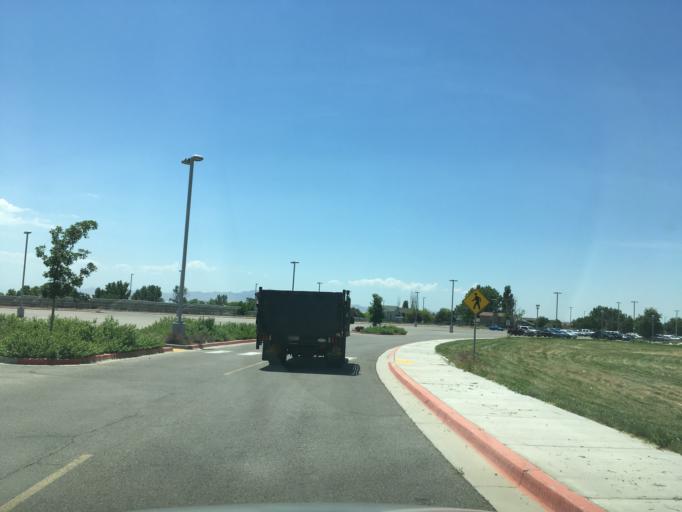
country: US
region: Utah
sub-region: Davis County
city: Hill Air Force Bace
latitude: 41.0983
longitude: -111.9803
